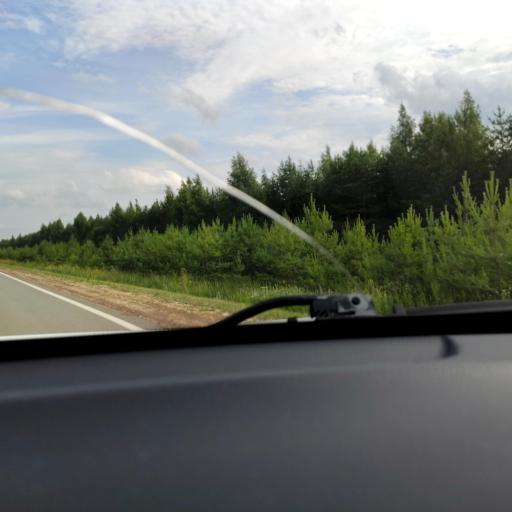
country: RU
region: Tatarstan
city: Sviyazhsk
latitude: 55.7347
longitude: 48.7394
